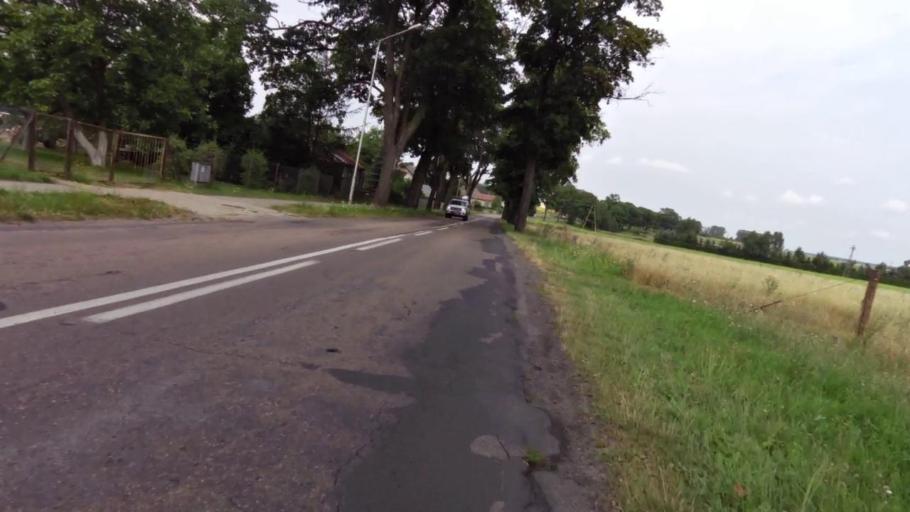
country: PL
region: West Pomeranian Voivodeship
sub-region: Powiat drawski
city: Drawsko Pomorskie
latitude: 53.5421
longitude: 15.8143
